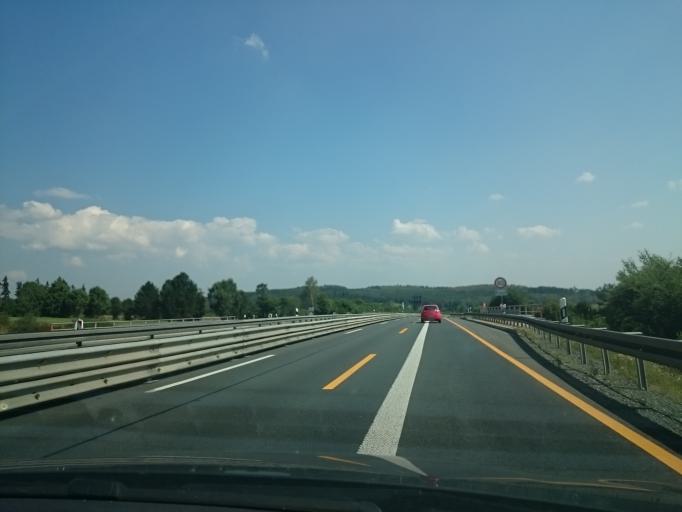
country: DE
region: Bavaria
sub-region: Upper Franconia
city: Trogen
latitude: 50.3942
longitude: 11.9910
